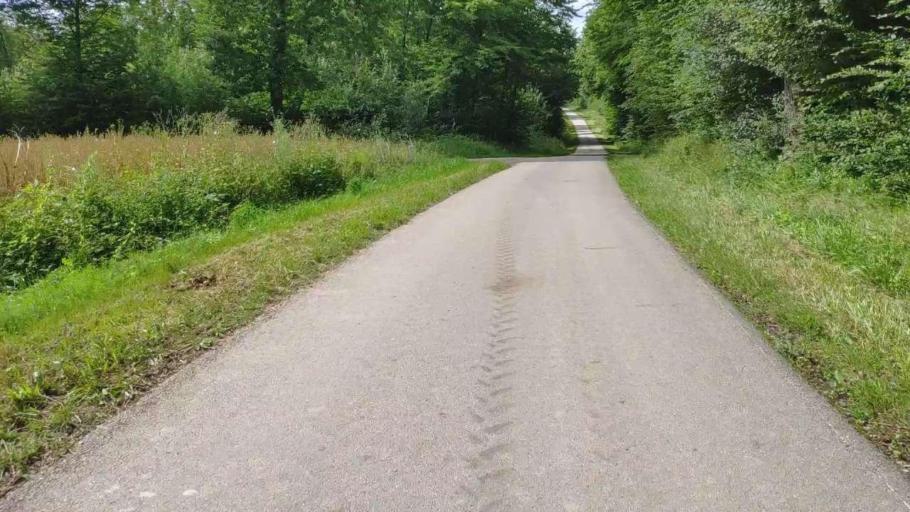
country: FR
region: Franche-Comte
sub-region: Departement du Jura
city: Bletterans
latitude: 46.8083
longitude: 5.4412
